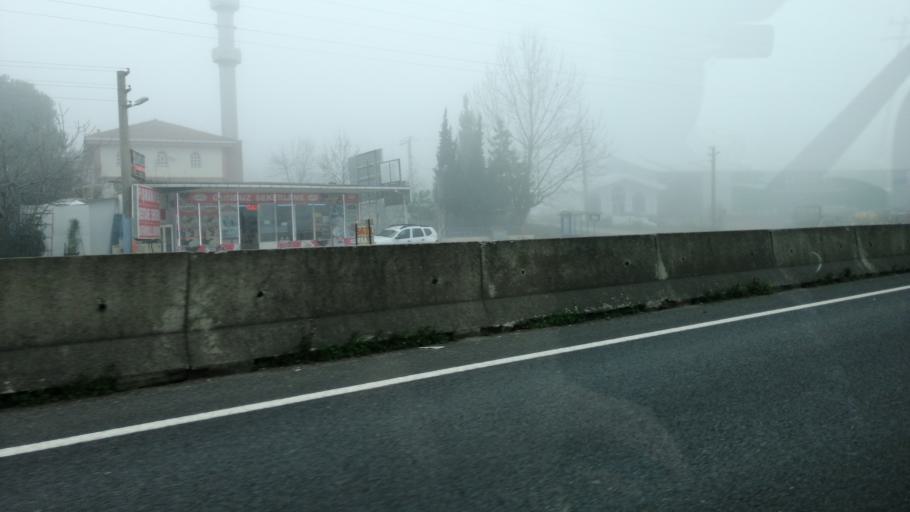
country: TR
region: Yalova
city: Ciftlikkoy
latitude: 40.6694
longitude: 29.3380
